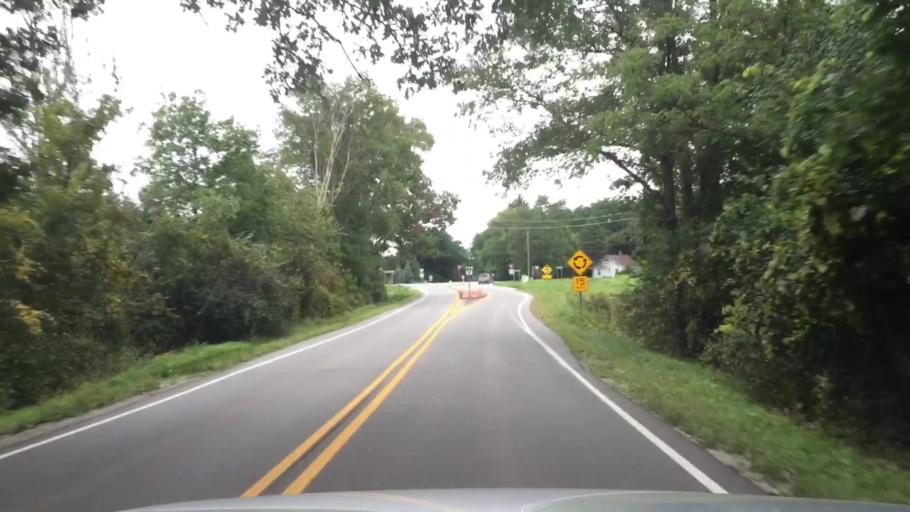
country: US
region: Michigan
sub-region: Washtenaw County
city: Ypsilanti
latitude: 42.2007
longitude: -83.6244
